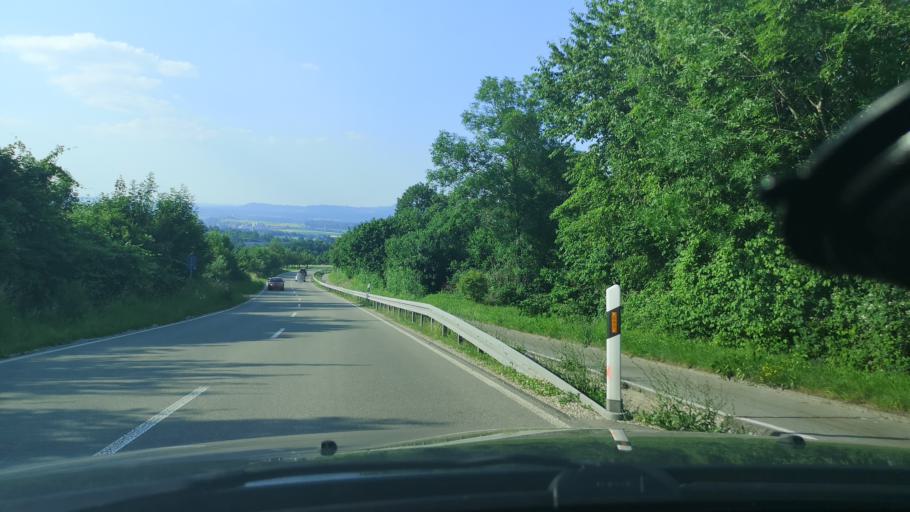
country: DE
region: Baden-Wuerttemberg
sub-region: Regierungsbezirk Stuttgart
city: Schlat
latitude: 48.6416
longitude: 9.7026
